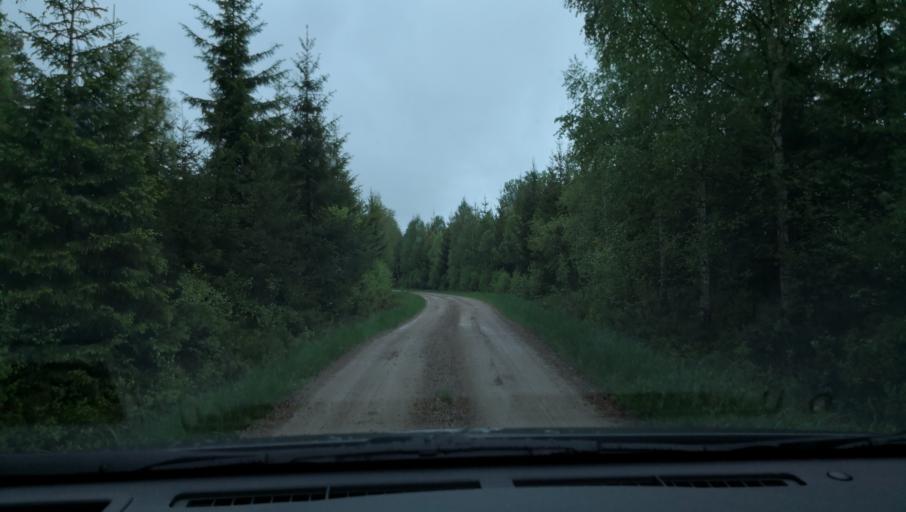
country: SE
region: Uppsala
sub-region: Enkopings Kommun
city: Orsundsbro
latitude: 59.9227
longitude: 17.3412
